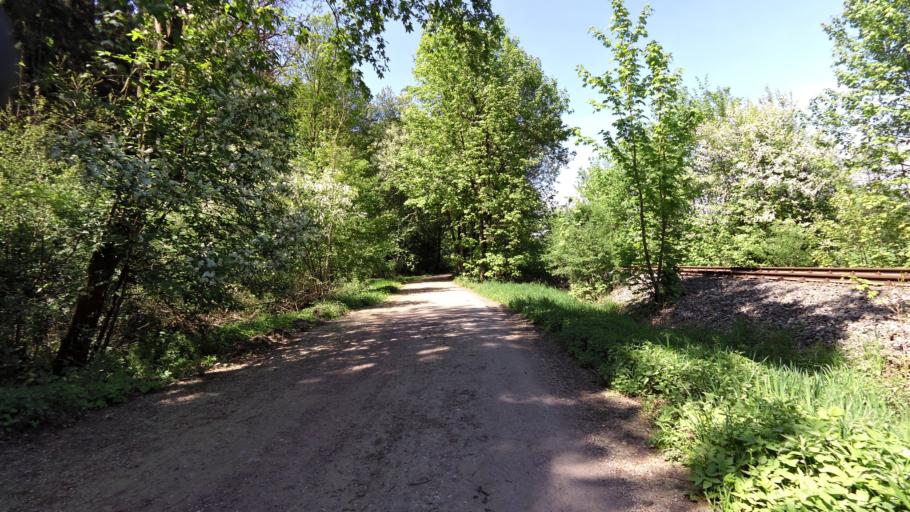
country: DE
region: Bavaria
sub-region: Lower Bavaria
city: Weihmichl
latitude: 48.5642
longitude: 12.0858
